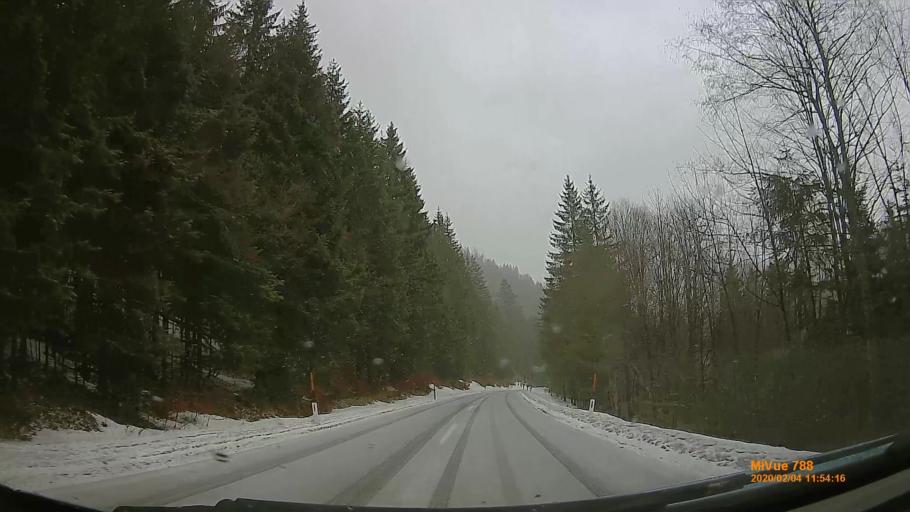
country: AT
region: Styria
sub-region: Politischer Bezirk Bruck-Muerzzuschlag
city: Muerzsteg
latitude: 47.7517
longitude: 15.4986
